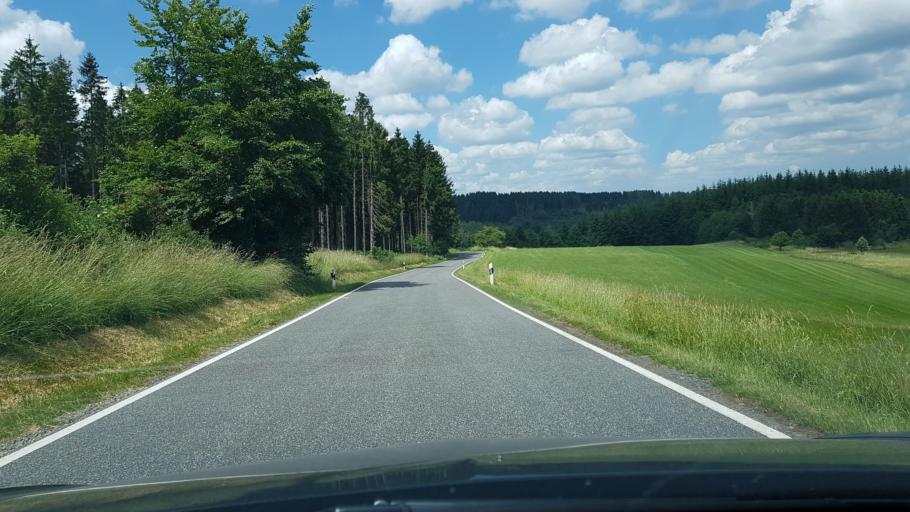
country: DE
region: Rheinland-Pfalz
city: Siebenbach
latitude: 50.3926
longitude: 7.0522
